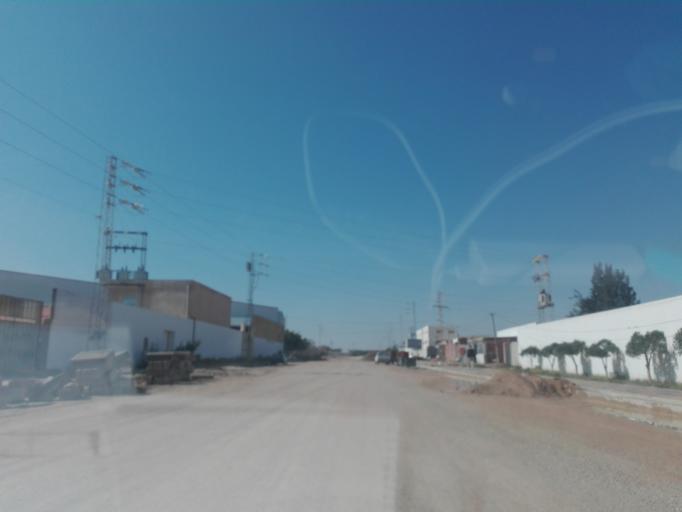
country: TN
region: Safaqis
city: Sfax
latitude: 34.7283
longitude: 10.5147
